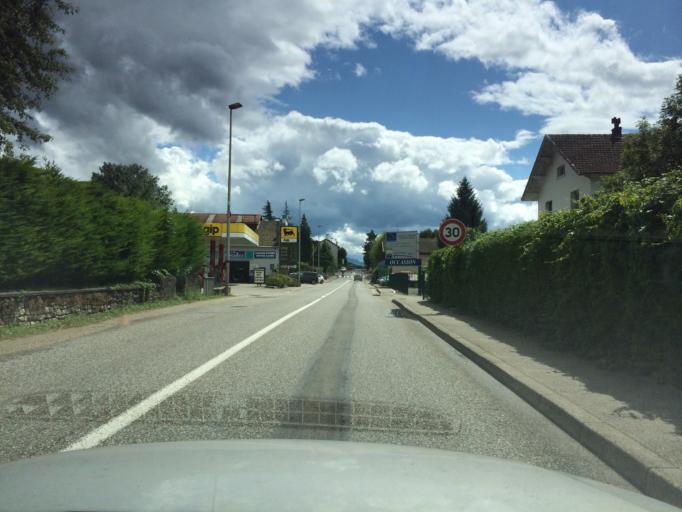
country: FR
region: Rhone-Alpes
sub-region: Departement de la Haute-Savoie
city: Versonnex
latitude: 45.9626
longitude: 5.8368
